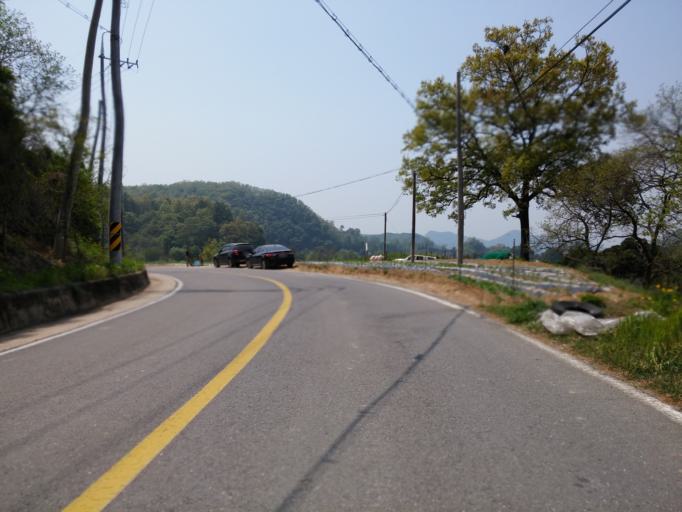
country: KR
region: Chungcheongbuk-do
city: Okcheon
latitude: 36.4467
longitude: 127.5855
